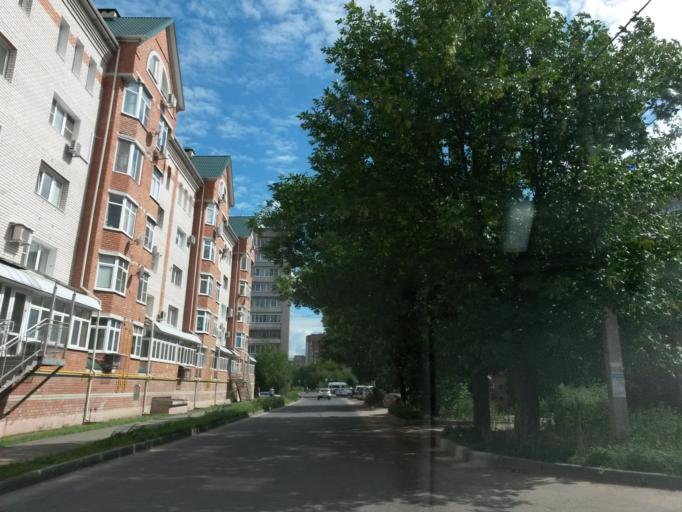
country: RU
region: Ivanovo
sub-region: Gorod Ivanovo
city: Ivanovo
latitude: 56.9922
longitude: 40.9710
